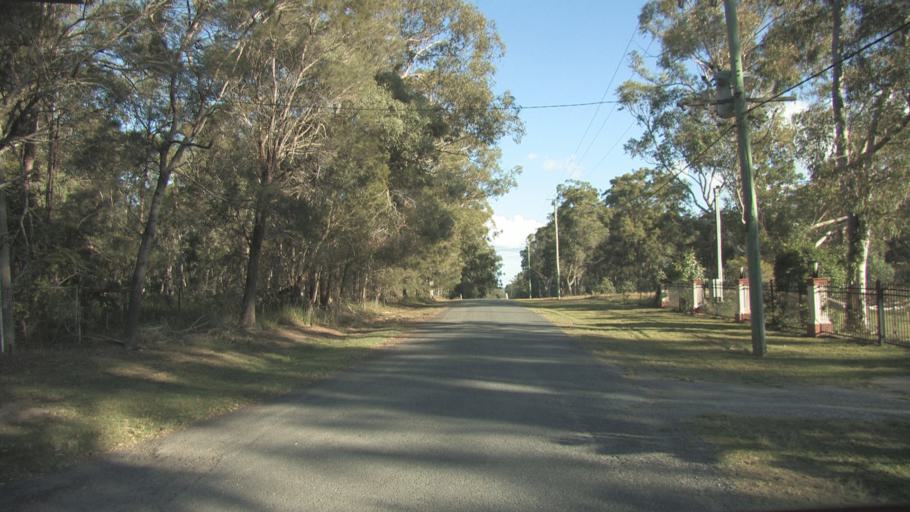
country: AU
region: Queensland
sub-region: Gold Coast
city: Yatala
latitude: -27.6644
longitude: 153.2452
